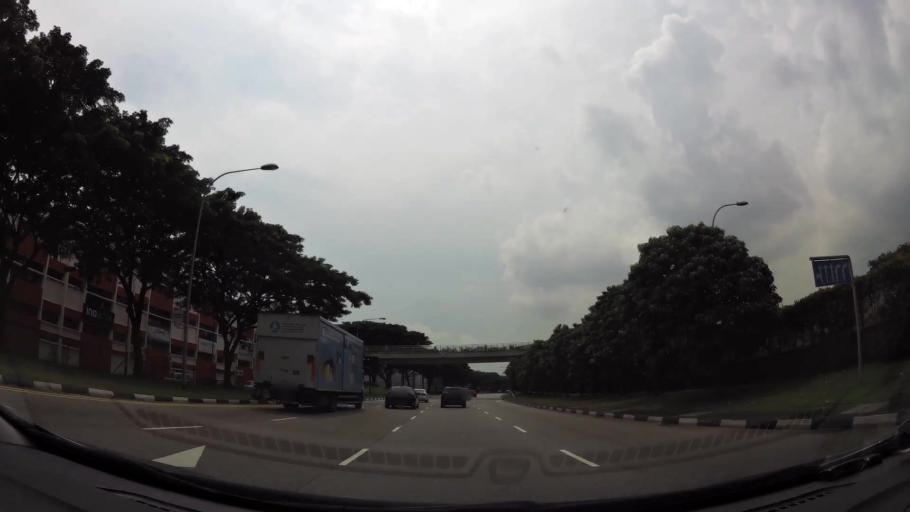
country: SG
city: Singapore
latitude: 1.3396
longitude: 103.8976
